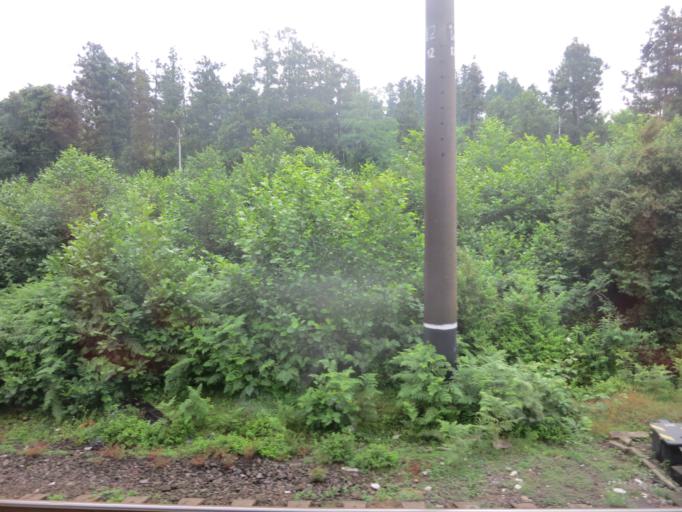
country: GE
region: Guria
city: Urek'i
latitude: 41.9951
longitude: 41.7804
